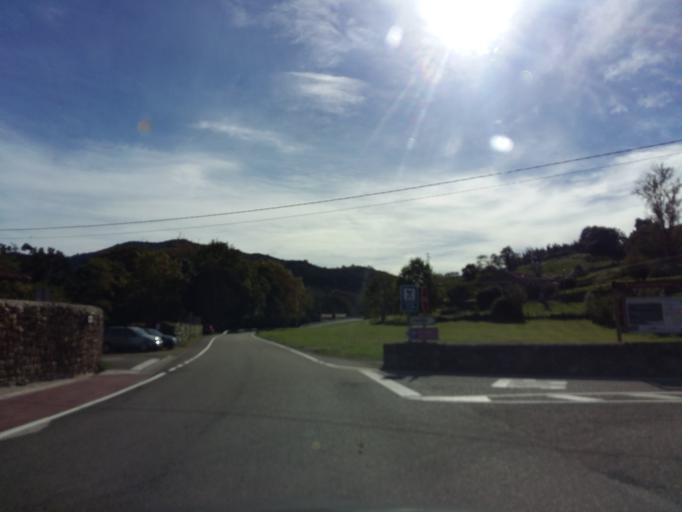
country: ES
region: Cantabria
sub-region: Provincia de Cantabria
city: San Vicente de la Barquera
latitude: 43.3048
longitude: -4.4669
